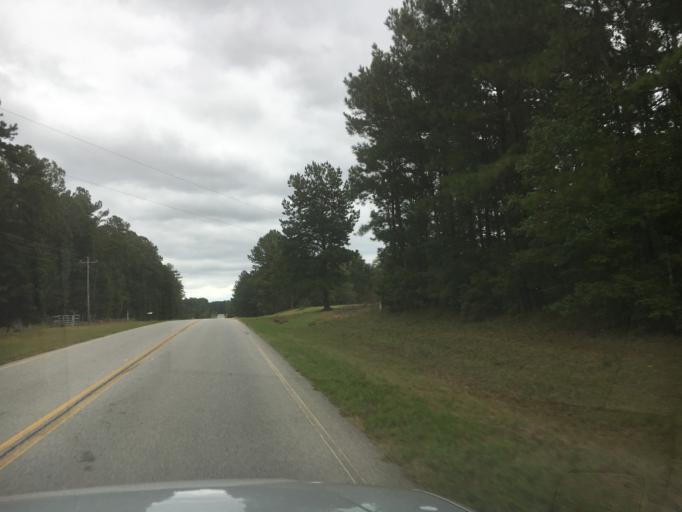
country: US
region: Georgia
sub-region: Lincoln County
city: Lincolnton
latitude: 33.7381
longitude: -82.5505
